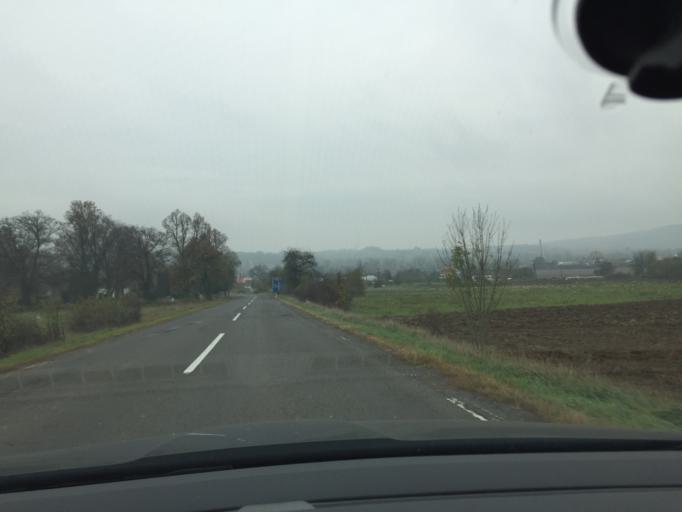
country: SK
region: Banskobystricky
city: Velky Krtis
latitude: 48.2380
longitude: 19.4245
